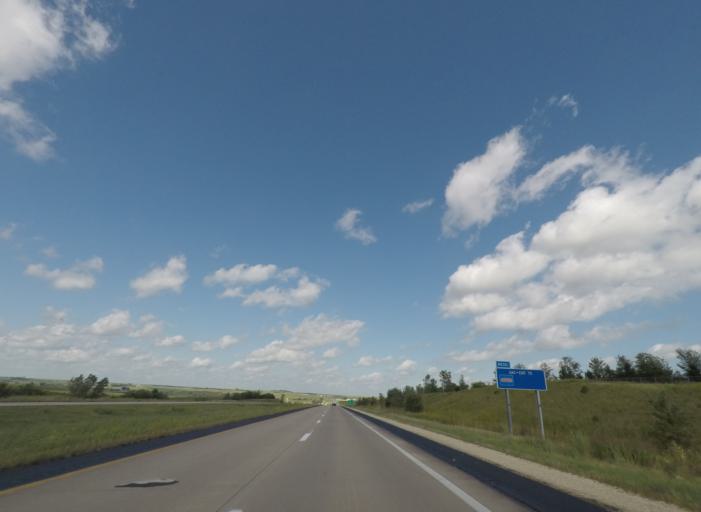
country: US
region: Iowa
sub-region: Dubuque County
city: Cascade
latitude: 42.2973
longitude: -91.0324
